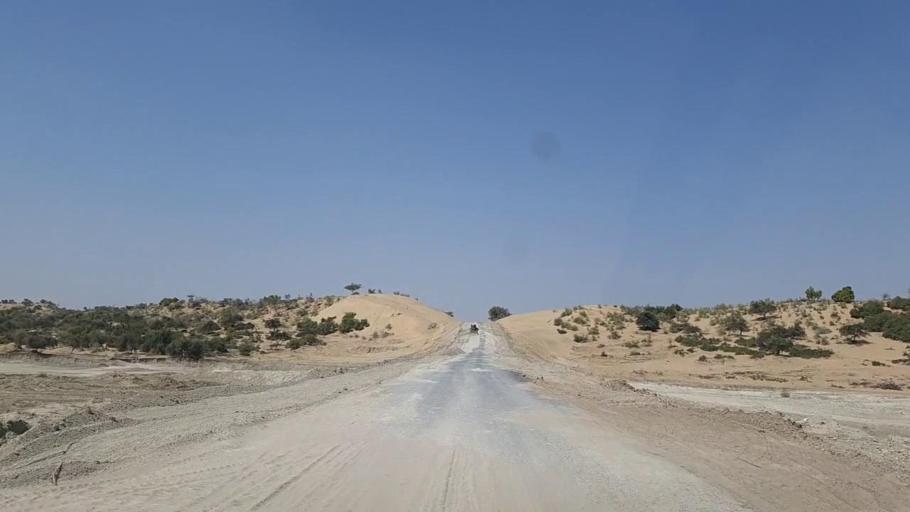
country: PK
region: Sindh
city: Diplo
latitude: 24.5863
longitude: 69.5596
